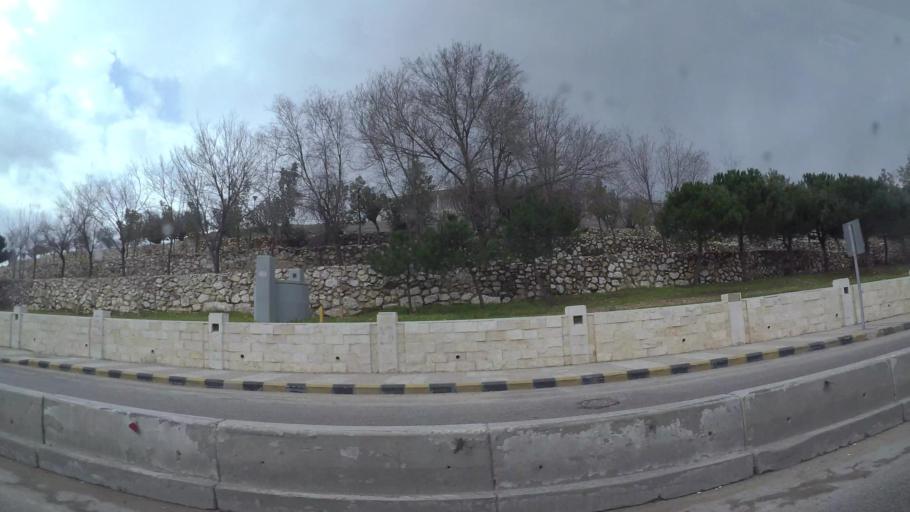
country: JO
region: Amman
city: Wadi as Sir
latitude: 31.9806
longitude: 35.8349
